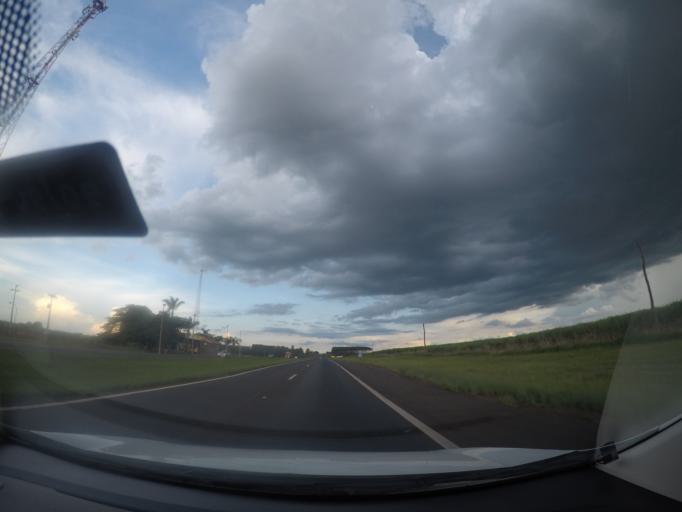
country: BR
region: Sao Paulo
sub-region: Ibate
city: Ibate
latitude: -21.9132
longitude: -48.0446
